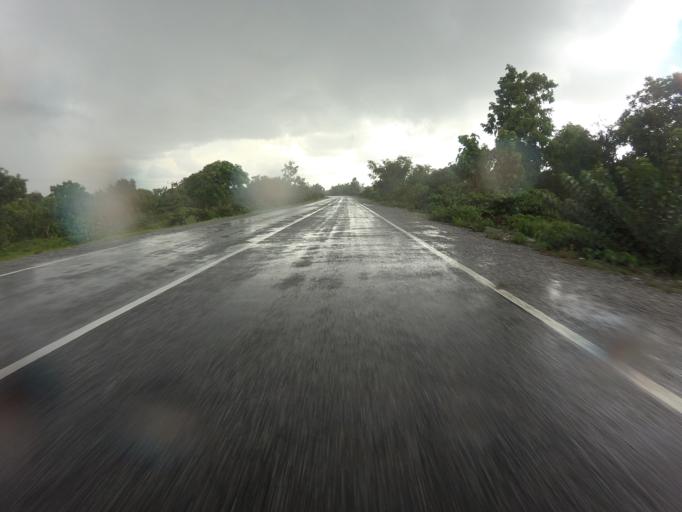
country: GH
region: Northern
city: Tamale
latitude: 9.1325
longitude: -1.5887
